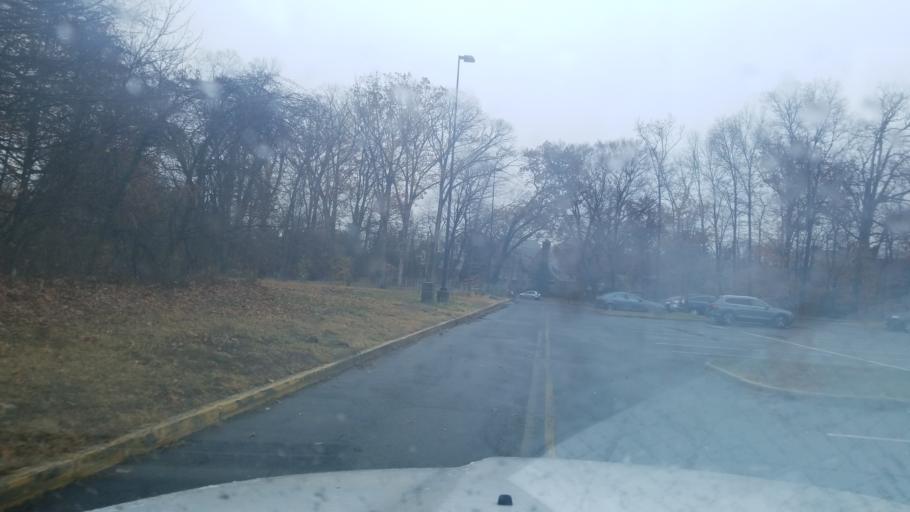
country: US
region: Maryland
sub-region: Montgomery County
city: Takoma Park
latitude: 38.9519
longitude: -77.0389
